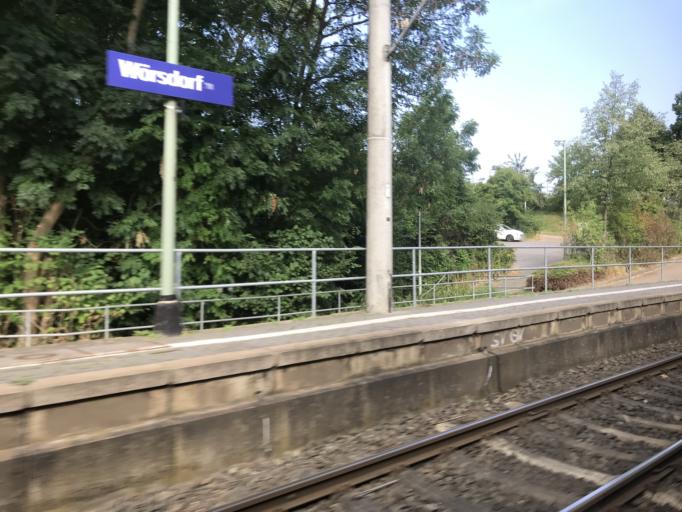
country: DE
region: Hesse
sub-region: Regierungsbezirk Darmstadt
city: Idstein
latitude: 50.2449
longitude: 8.2492
